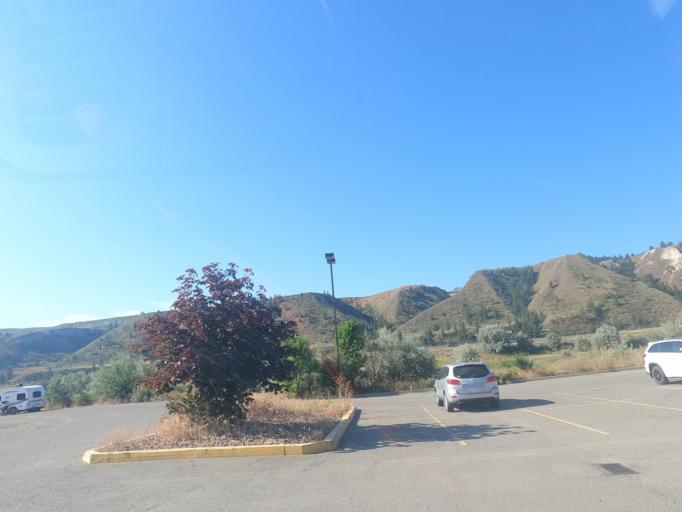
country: CA
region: British Columbia
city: Kamloops
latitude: 50.6610
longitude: -120.1198
